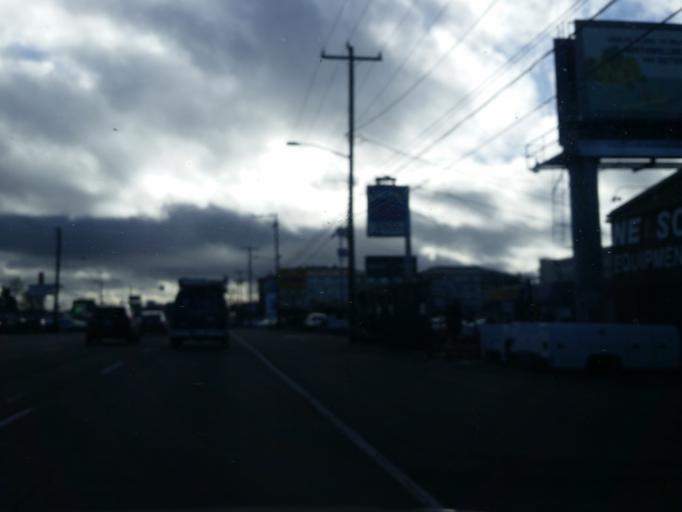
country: US
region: Washington
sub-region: King County
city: Shoreline
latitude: 47.7332
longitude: -122.3452
